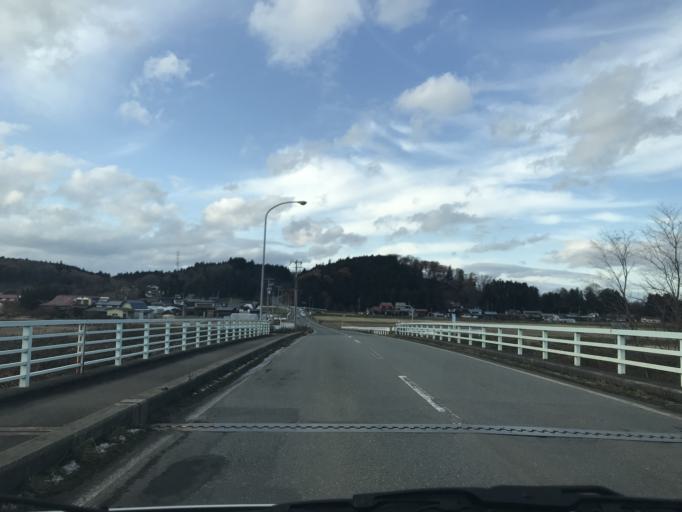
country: JP
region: Iwate
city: Mizusawa
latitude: 39.1665
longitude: 141.0896
